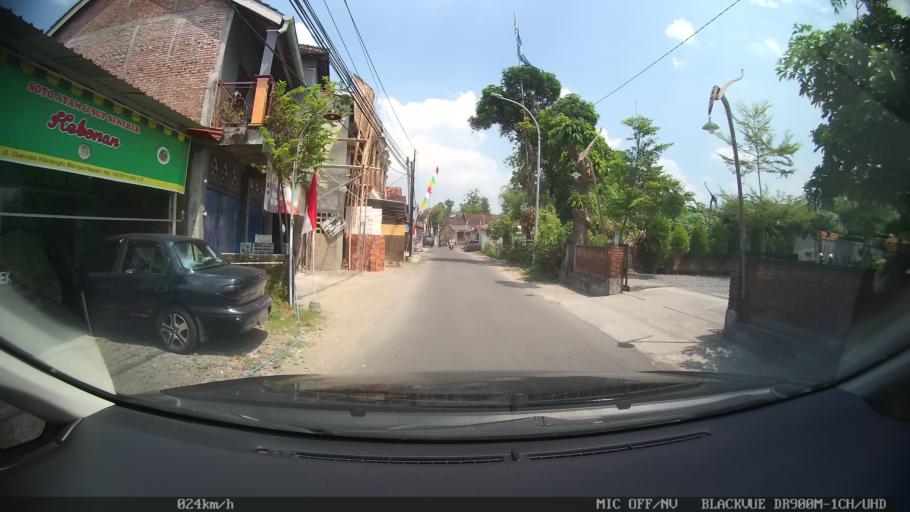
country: ID
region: Daerah Istimewa Yogyakarta
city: Yogyakarta
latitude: -7.8273
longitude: 110.4060
